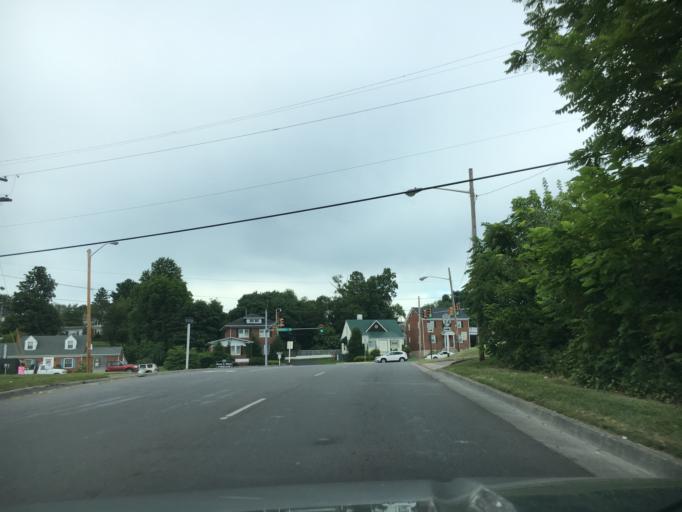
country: US
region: Virginia
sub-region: Roanoke County
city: Vinton
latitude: 37.2769
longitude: -79.8818
